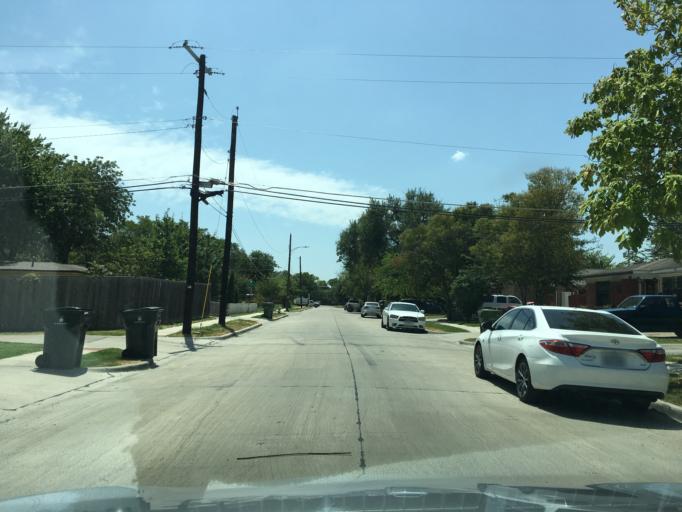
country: US
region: Texas
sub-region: Dallas County
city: Garland
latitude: 32.8957
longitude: -96.6295
